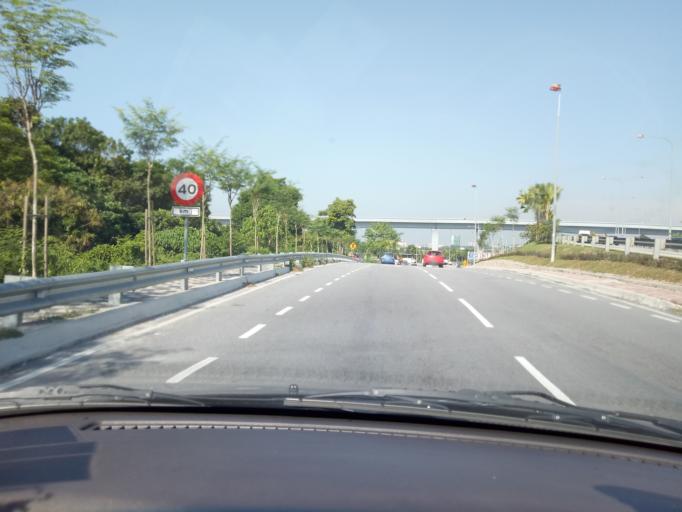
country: MY
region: Selangor
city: Kampong Baharu Balakong
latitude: 3.0040
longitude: 101.7841
